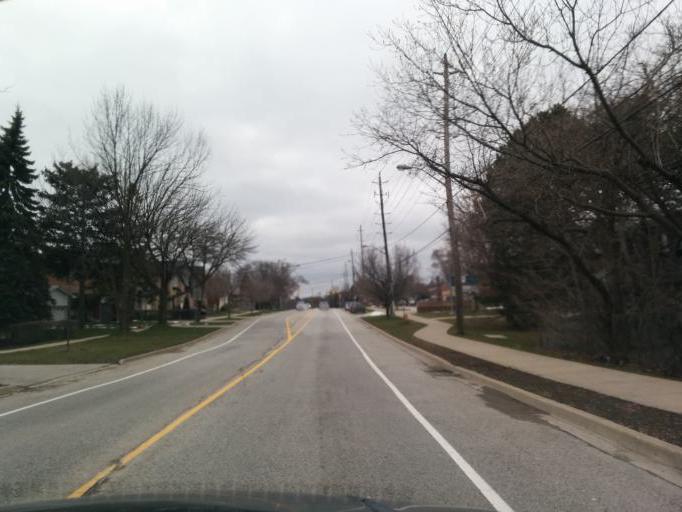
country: CA
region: Ontario
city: Etobicoke
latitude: 43.6353
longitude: -79.5063
